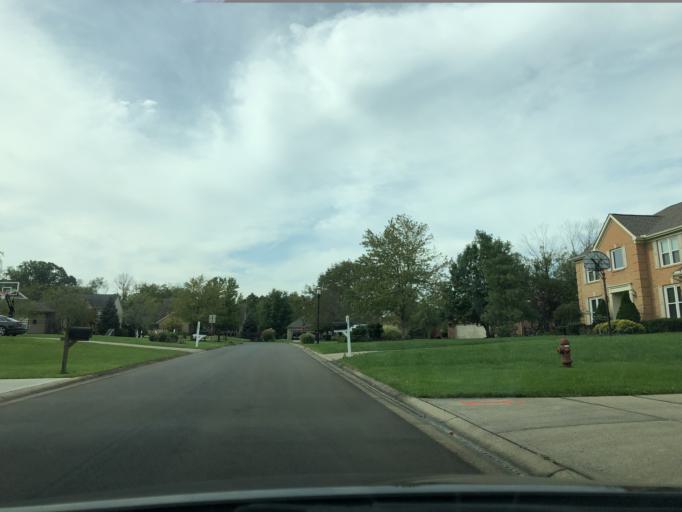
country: US
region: Ohio
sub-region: Hamilton County
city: Loveland
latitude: 39.2447
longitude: -84.2663
